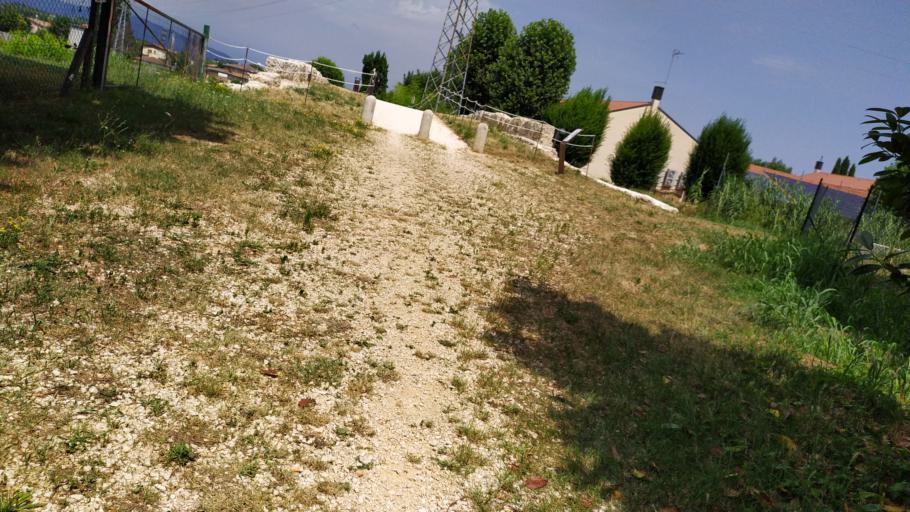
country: IT
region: Veneto
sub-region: Provincia di Treviso
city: Susegana
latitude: 45.8665
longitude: 12.2652
